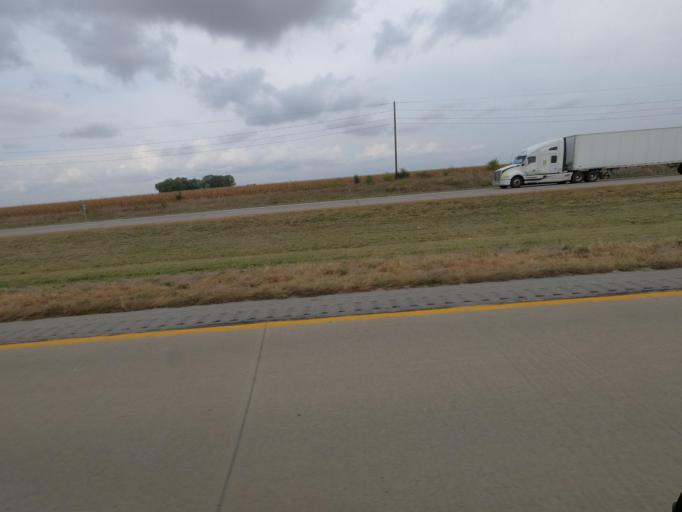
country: US
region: Iowa
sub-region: Jasper County
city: Monroe
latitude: 41.5621
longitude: -93.1534
